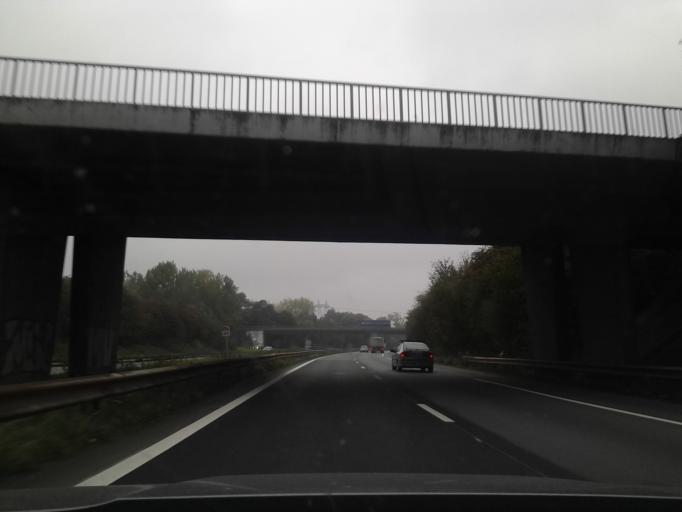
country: FR
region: Nord-Pas-de-Calais
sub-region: Departement du Nord
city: Marly
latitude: 50.3367
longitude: 3.5566
